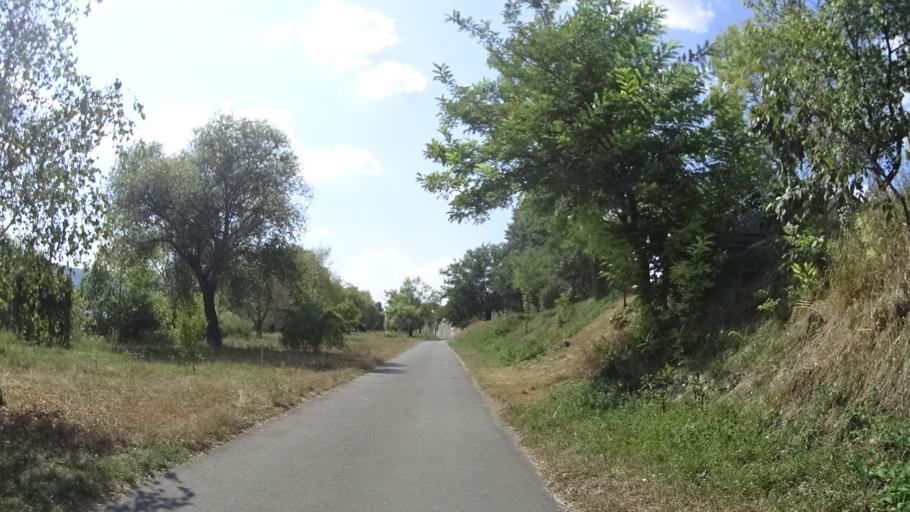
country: HU
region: Pest
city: Szob
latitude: 47.8151
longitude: 18.8719
